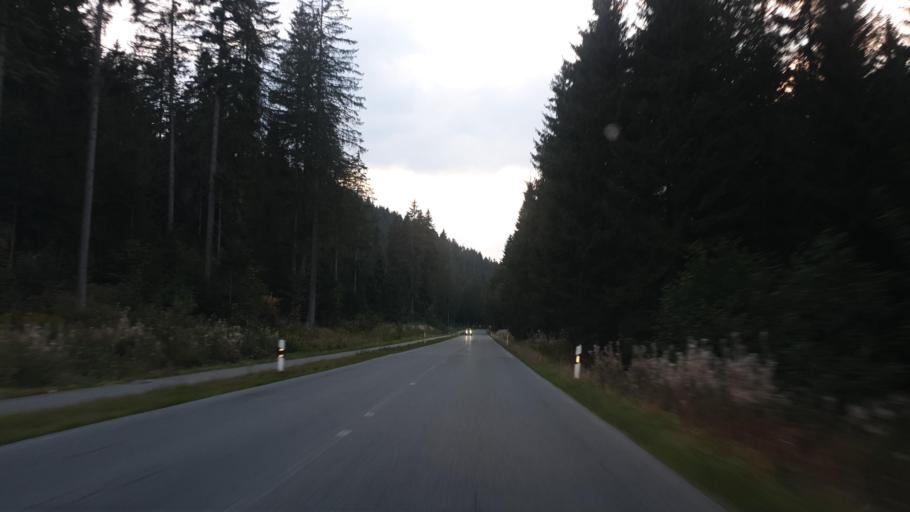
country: DE
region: Saxony
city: Sosa
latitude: 50.4375
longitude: 12.6423
